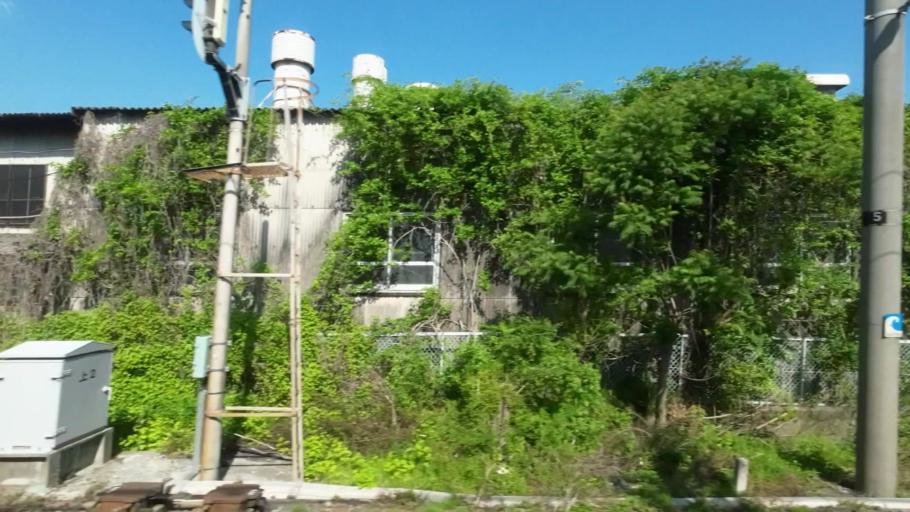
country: JP
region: Kagawa
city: Takamatsu-shi
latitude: 34.3400
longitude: 134.0091
